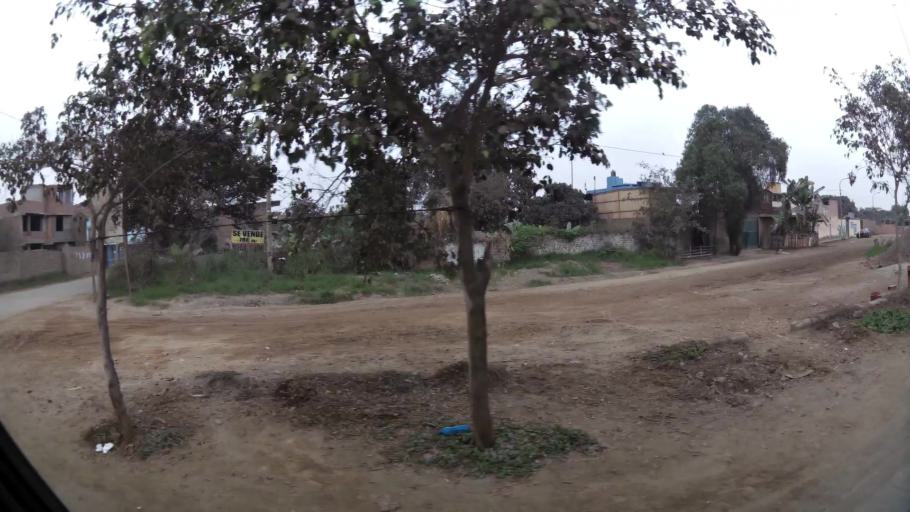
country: PE
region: Lima
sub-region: Lima
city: Urb. Santo Domingo
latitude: -11.8825
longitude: -77.0659
